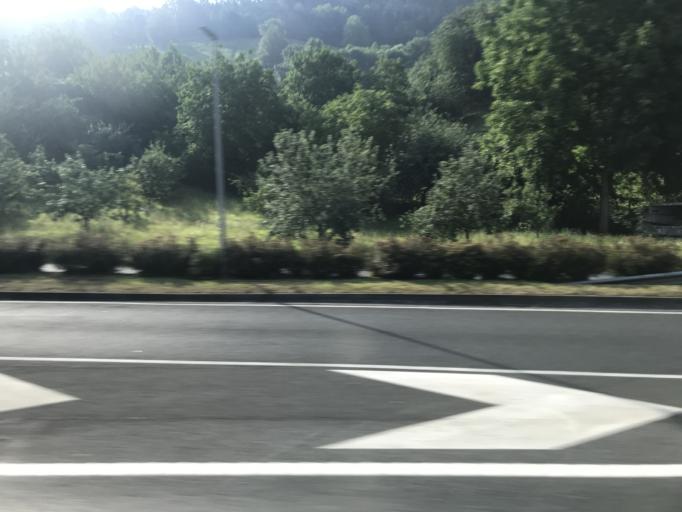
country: ES
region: Basque Country
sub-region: Provincia de Guipuzcoa
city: Villabona
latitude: 43.1763
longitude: -2.0562
